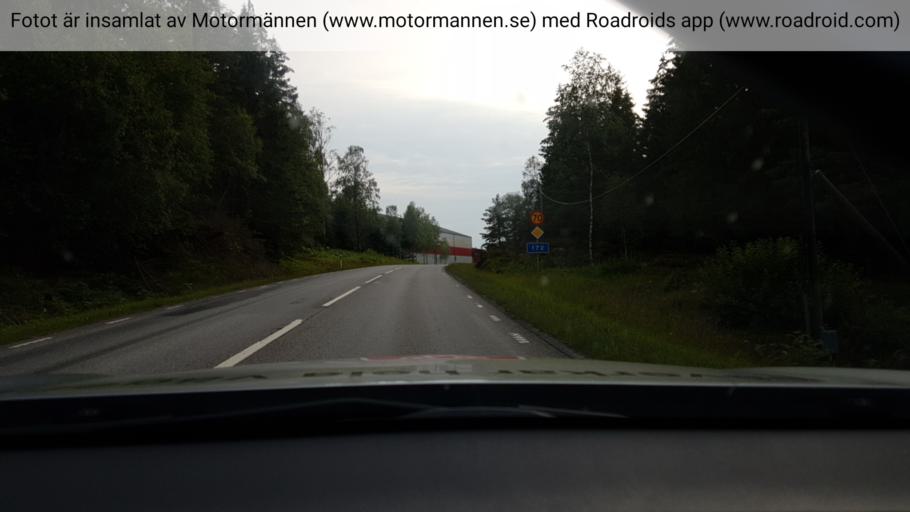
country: SE
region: Vaestra Goetaland
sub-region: Uddevalla Kommun
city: Uddevalla
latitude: 58.3761
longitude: 11.9828
